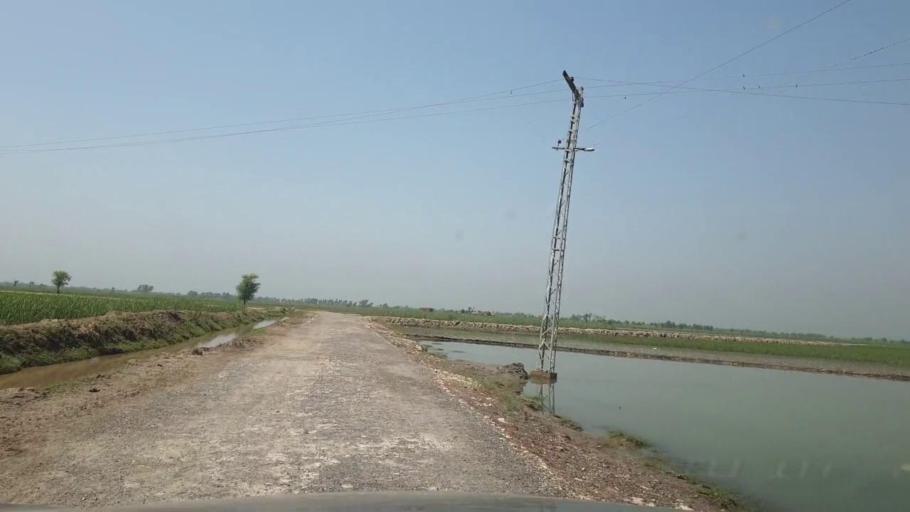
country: PK
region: Sindh
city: Warah
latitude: 27.4871
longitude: 67.7797
